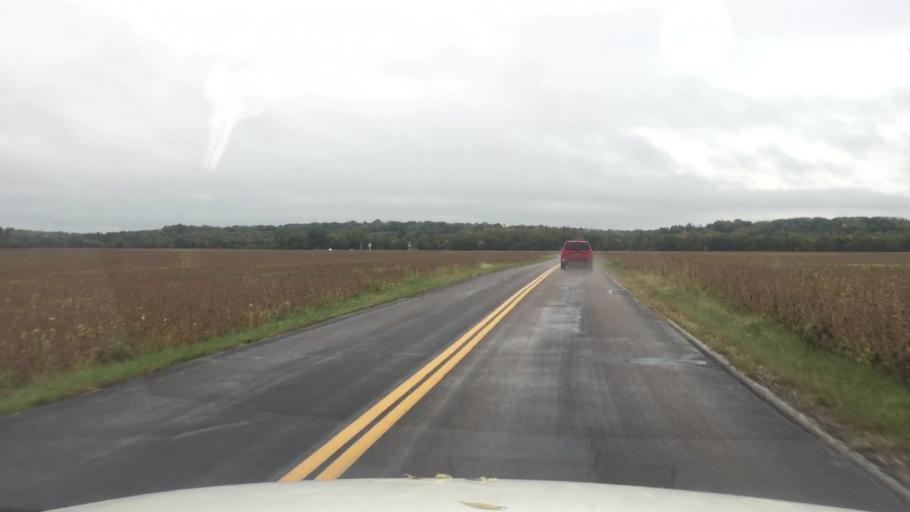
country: US
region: Missouri
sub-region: Boone County
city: Columbia
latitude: 38.8900
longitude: -92.4662
